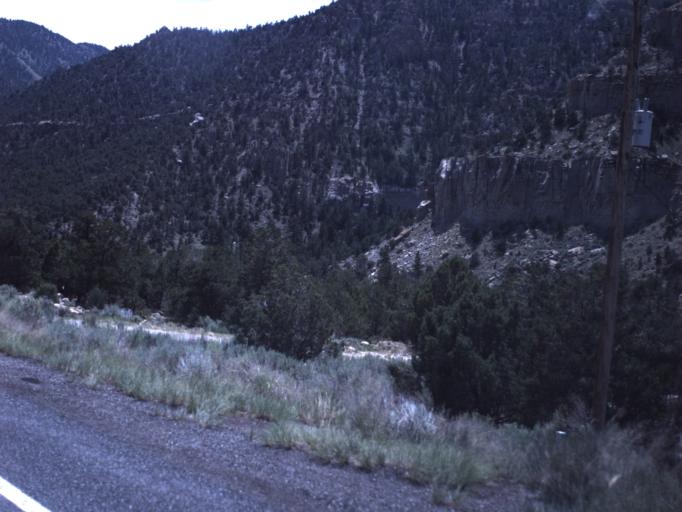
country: US
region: Utah
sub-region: Emery County
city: Huntington
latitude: 39.3971
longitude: -111.1099
